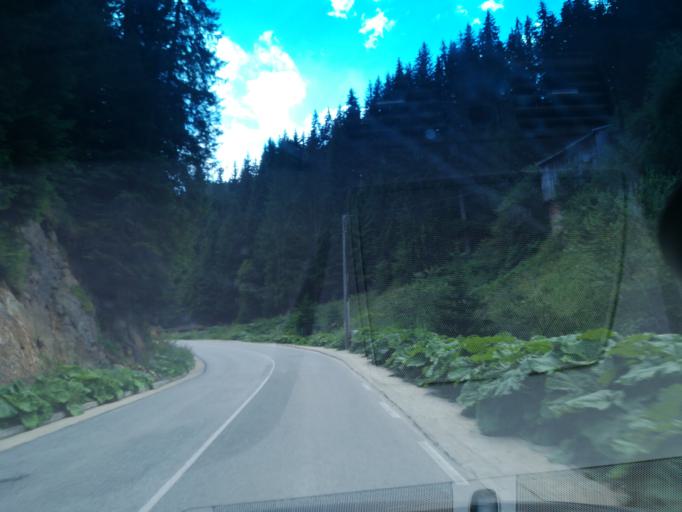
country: BG
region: Smolyan
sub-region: Obshtina Chepelare
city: Chepelare
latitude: 41.6586
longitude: 24.6327
